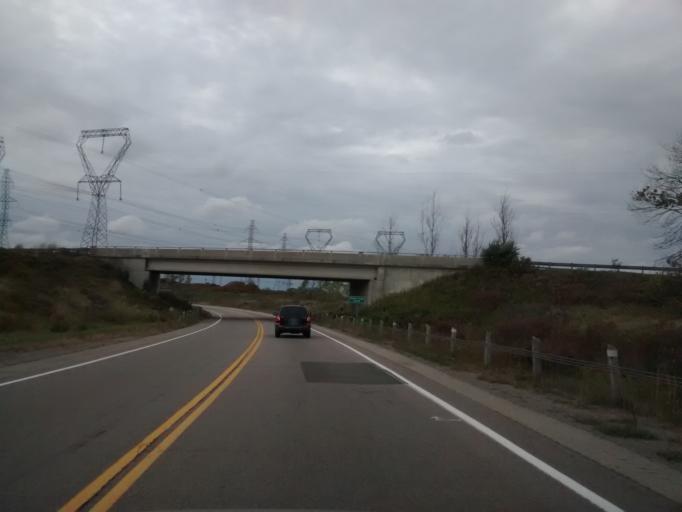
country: CA
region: Ontario
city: Ancaster
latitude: 43.0603
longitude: -79.9814
